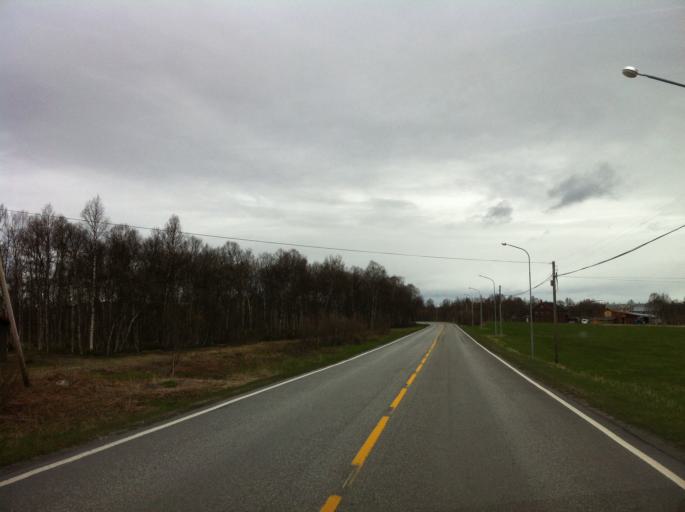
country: NO
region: Sor-Trondelag
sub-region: Tydal
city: Aas
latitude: 62.6427
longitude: 11.8865
